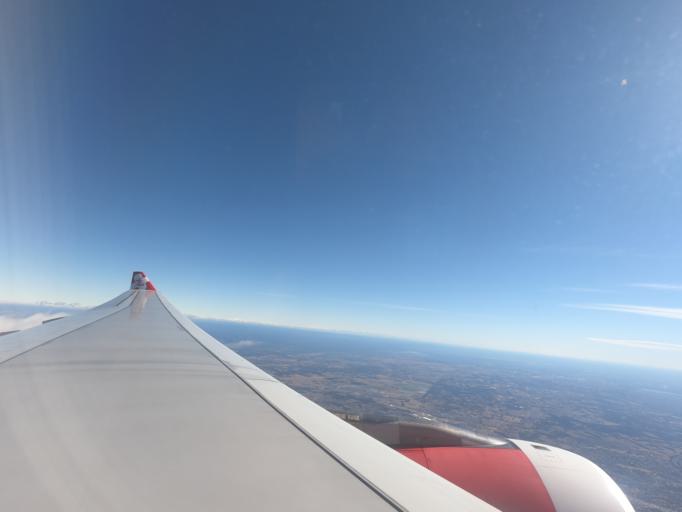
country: AU
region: New South Wales
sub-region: Campbelltown Municipality
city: Glen Alpine
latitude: -34.1207
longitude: 150.7861
